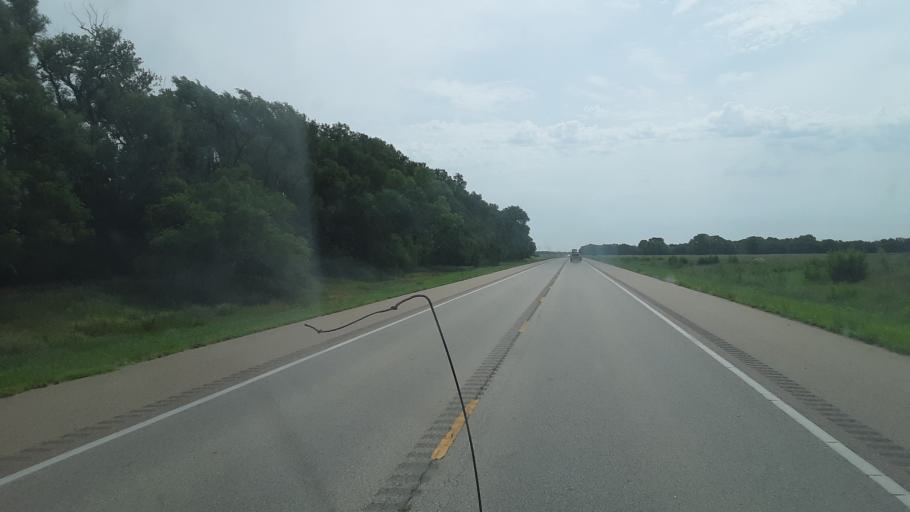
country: US
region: Kansas
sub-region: Reno County
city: Nickerson
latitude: 37.9846
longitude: -98.2431
